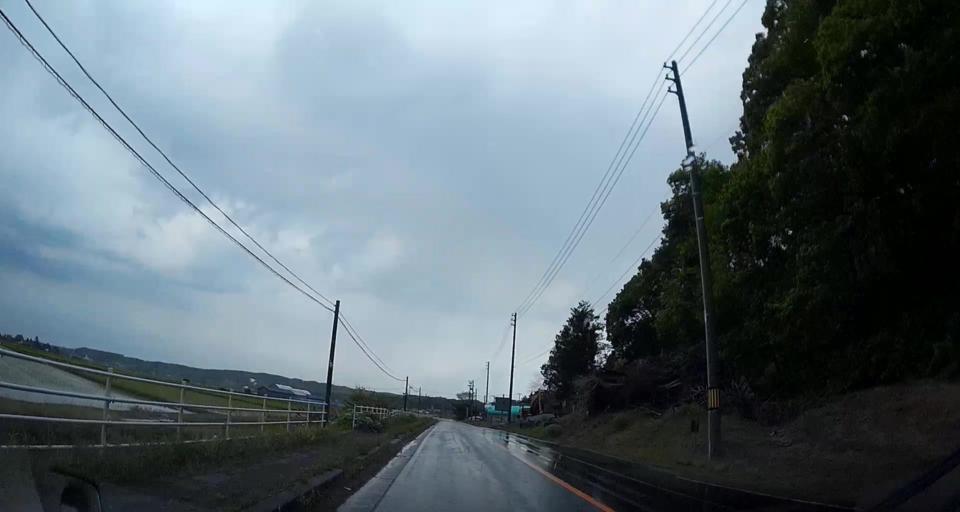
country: JP
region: Hokkaido
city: Chitose
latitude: 42.7361
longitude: 141.8963
